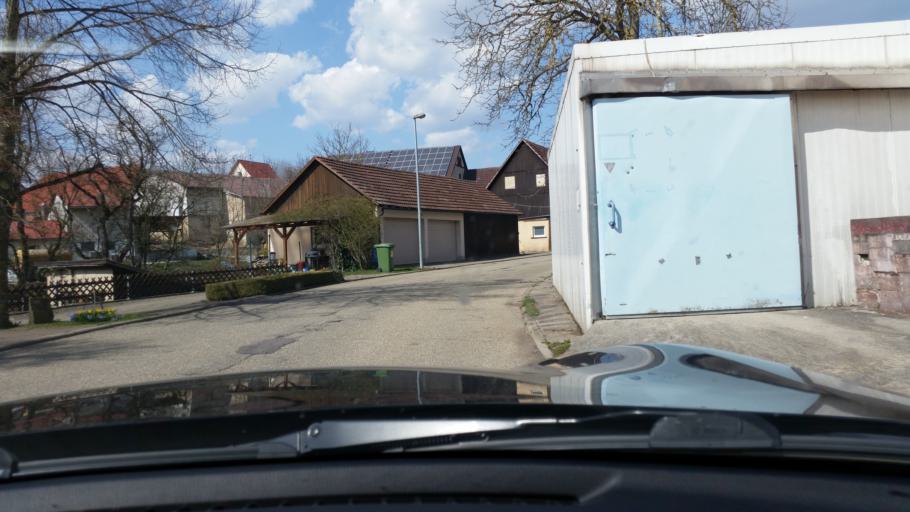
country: DE
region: Baden-Wuerttemberg
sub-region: Regierungsbezirk Stuttgart
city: Mulfingen
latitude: 49.2718
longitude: 9.7792
